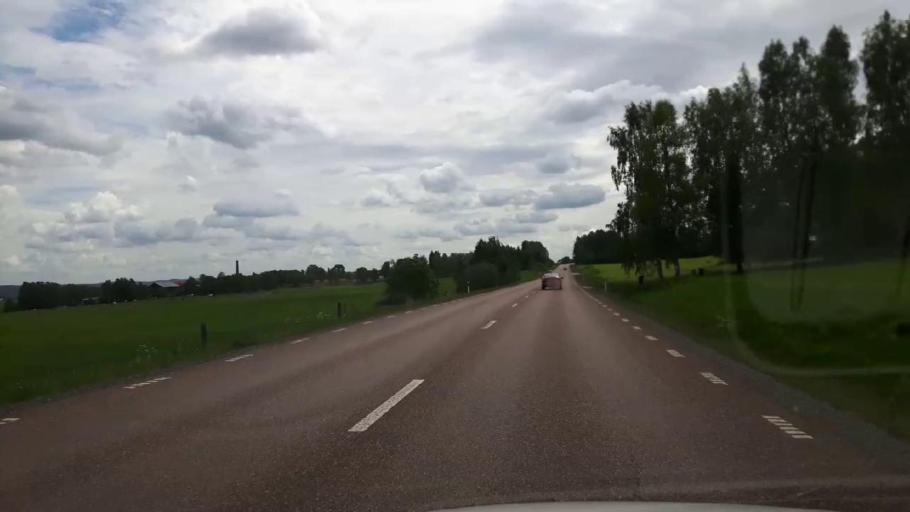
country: SE
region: Dalarna
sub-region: Hedemora Kommun
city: Hedemora
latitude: 60.3085
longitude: 15.9722
